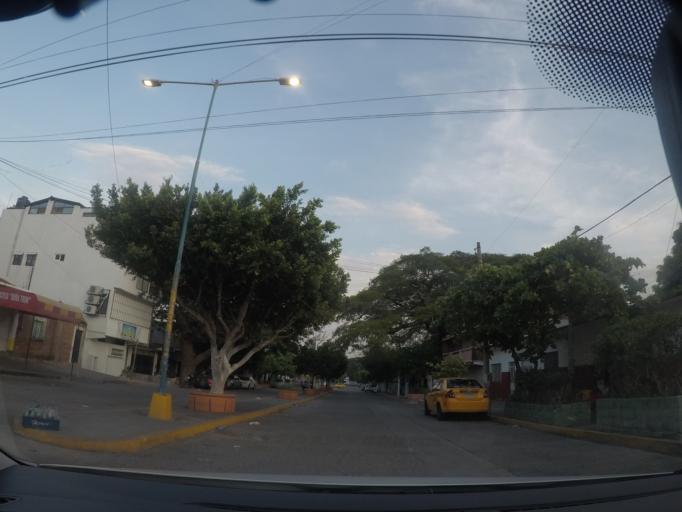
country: MX
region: Oaxaca
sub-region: Salina Cruz
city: Salina Cruz
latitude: 16.1847
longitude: -95.1987
